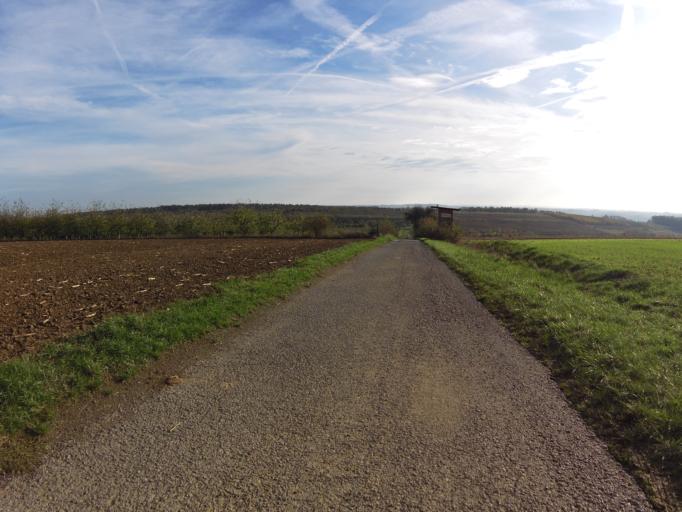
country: DE
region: Bavaria
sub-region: Regierungsbezirk Unterfranken
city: Sommerhausen
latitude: 49.7145
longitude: 10.0388
